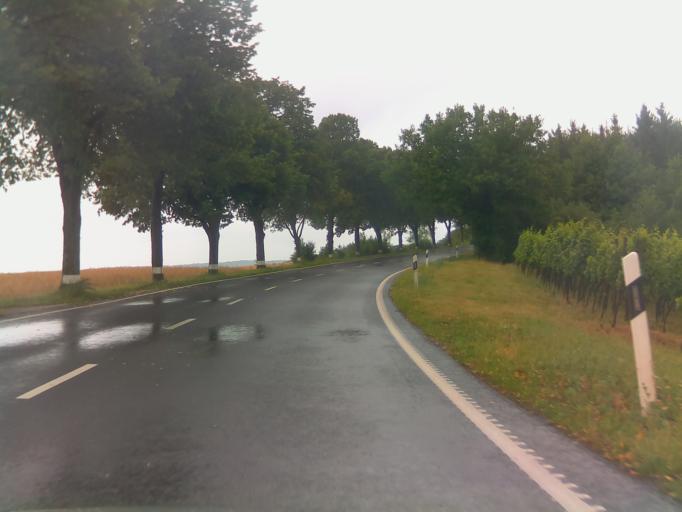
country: LU
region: Grevenmacher
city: Schengen
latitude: 49.4726
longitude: 6.3357
